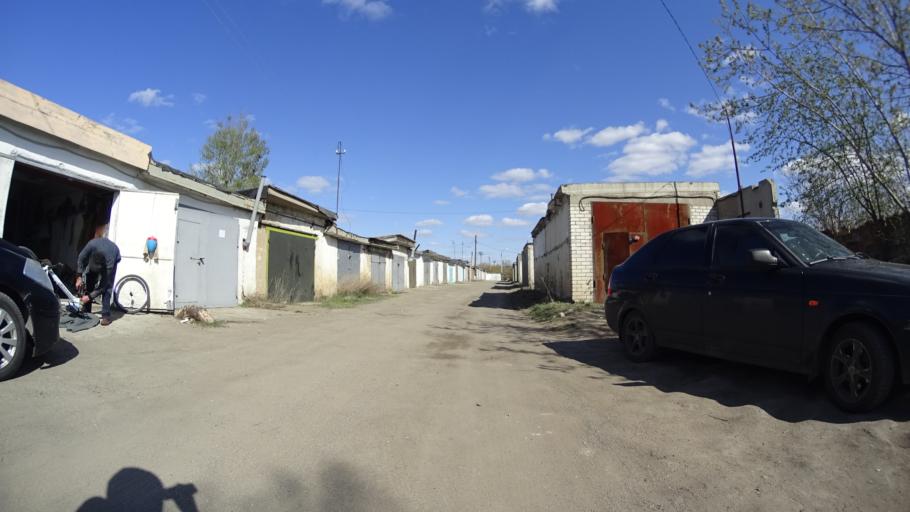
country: RU
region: Chelyabinsk
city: Troitsk
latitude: 54.0828
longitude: 61.5280
